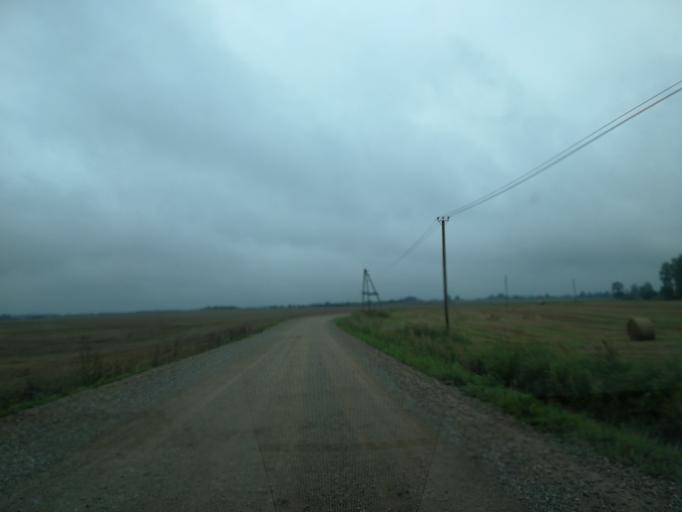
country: LV
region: Vilanu
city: Vilani
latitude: 56.3742
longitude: 27.0448
